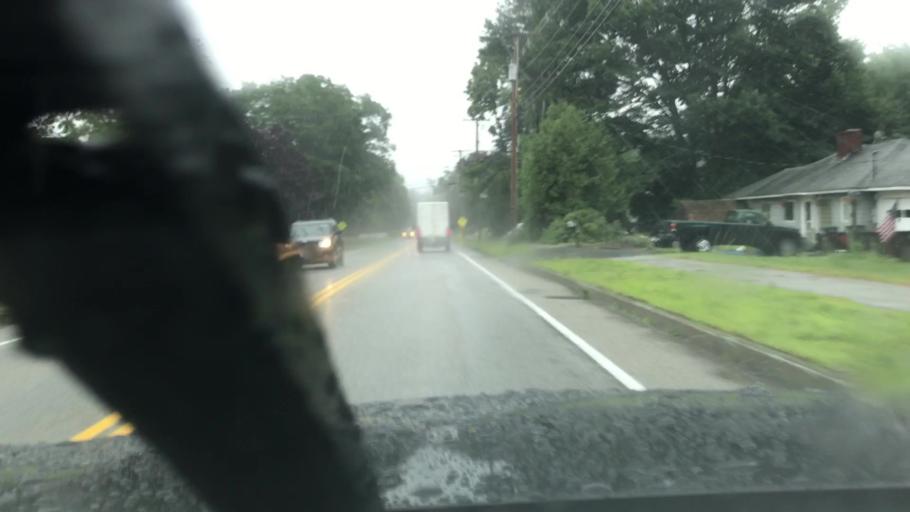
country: US
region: Maine
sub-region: York County
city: Kennebunk
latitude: 43.3953
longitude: -70.5497
